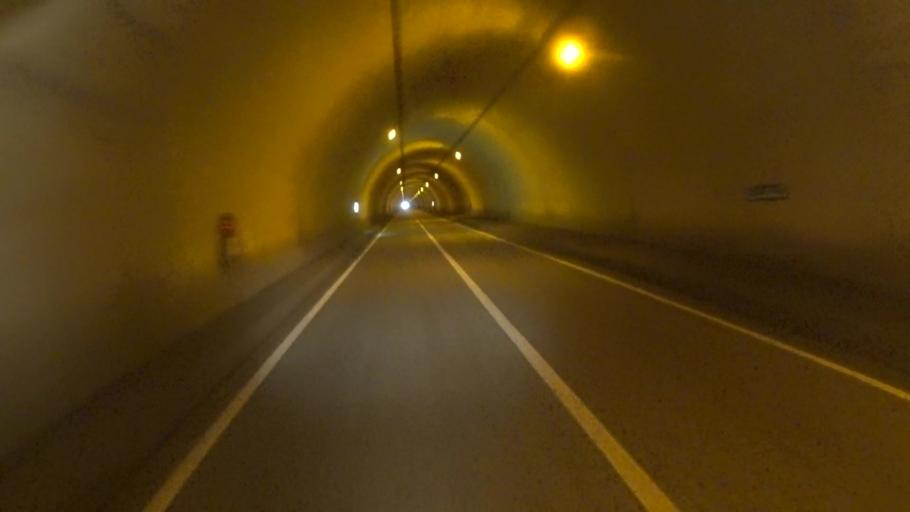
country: JP
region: Kyoto
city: Maizuru
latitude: 35.5185
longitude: 135.3704
